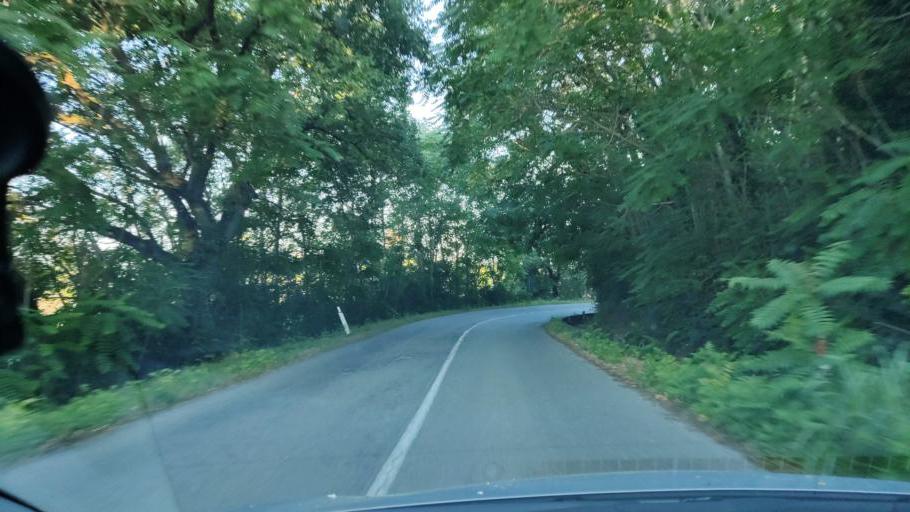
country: IT
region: Umbria
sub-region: Provincia di Terni
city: Giove
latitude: 42.5047
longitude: 12.3132
